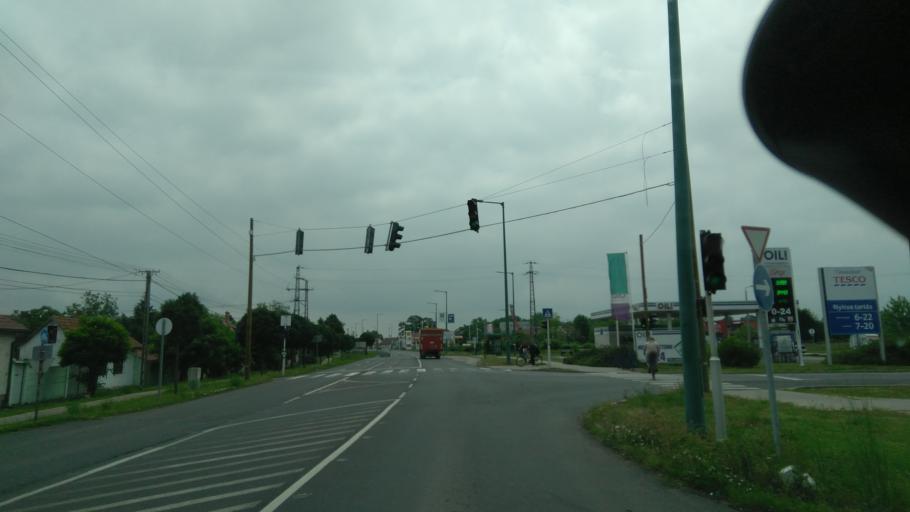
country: HU
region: Bekes
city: Gyula
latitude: 46.6424
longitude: 21.2600
